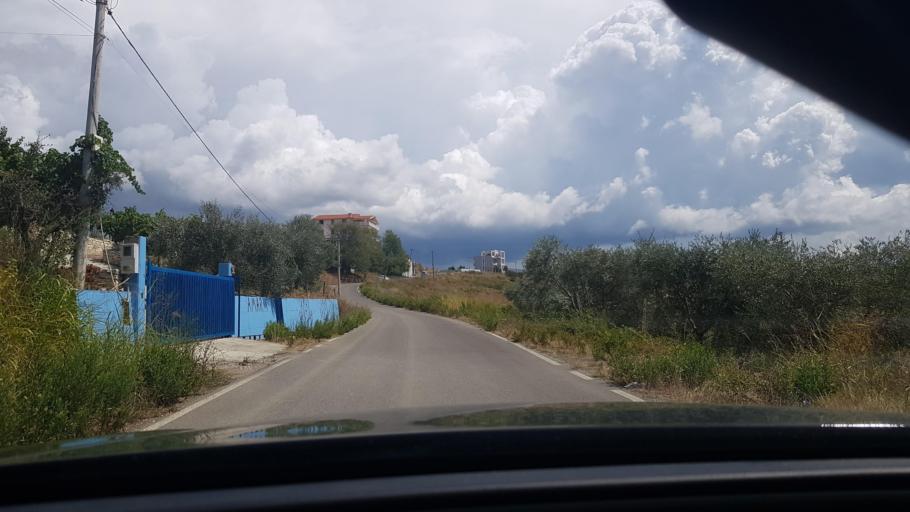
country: AL
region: Durres
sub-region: Rrethi i Durresit
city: Rrashbull
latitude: 41.2950
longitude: 19.5324
